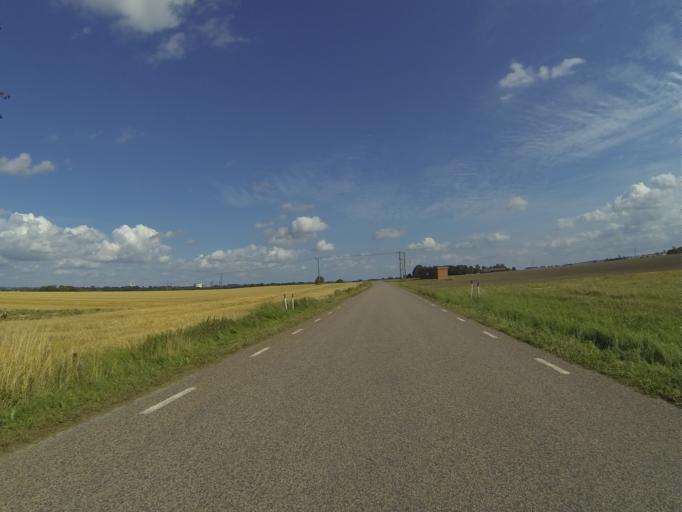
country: SE
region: Skane
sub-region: Lunds Kommun
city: Lund
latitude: 55.7773
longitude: 13.2144
